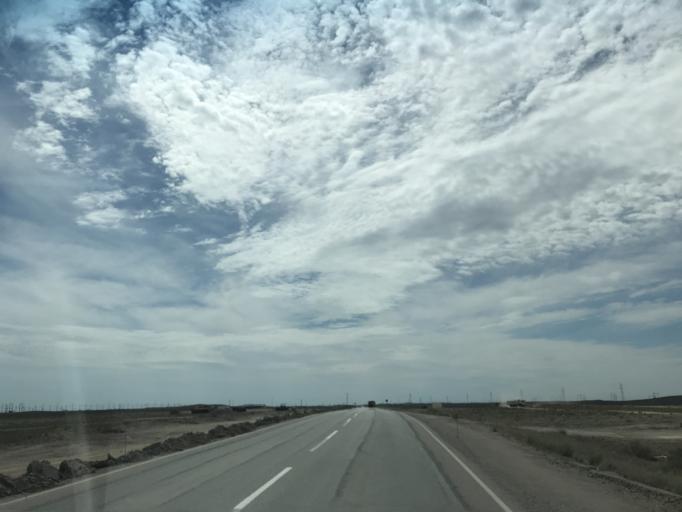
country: KZ
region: Almaty Oblysy
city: Ulken
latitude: 45.2362
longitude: 73.8341
